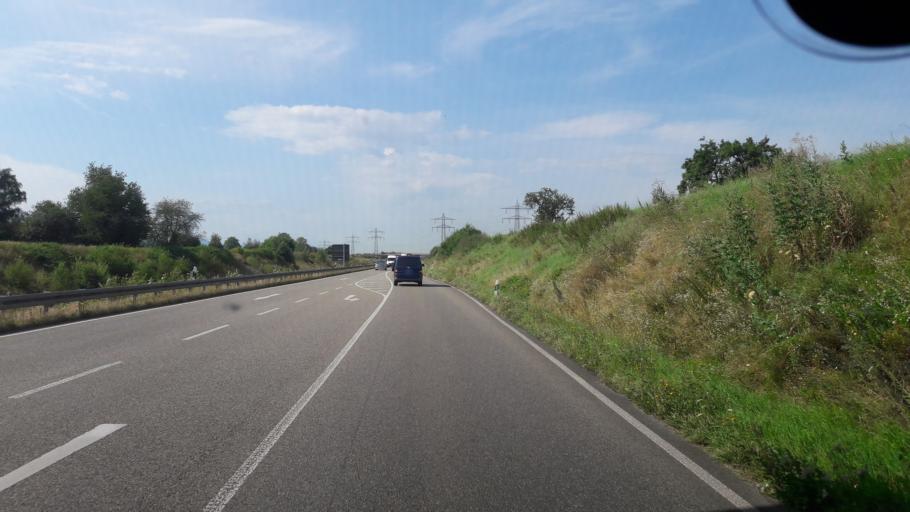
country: DE
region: Baden-Wuerttemberg
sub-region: Karlsruhe Region
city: Bietigheim
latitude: 48.9114
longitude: 8.2653
